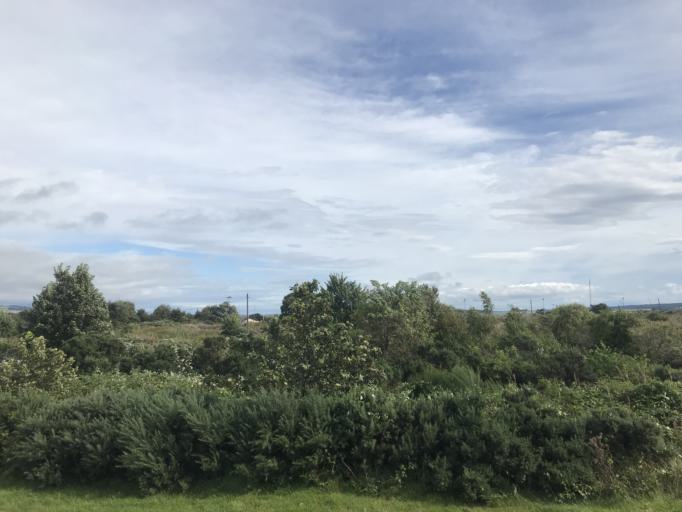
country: GB
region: Scotland
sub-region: Highland
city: Inverness
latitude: 57.4929
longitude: -4.2164
